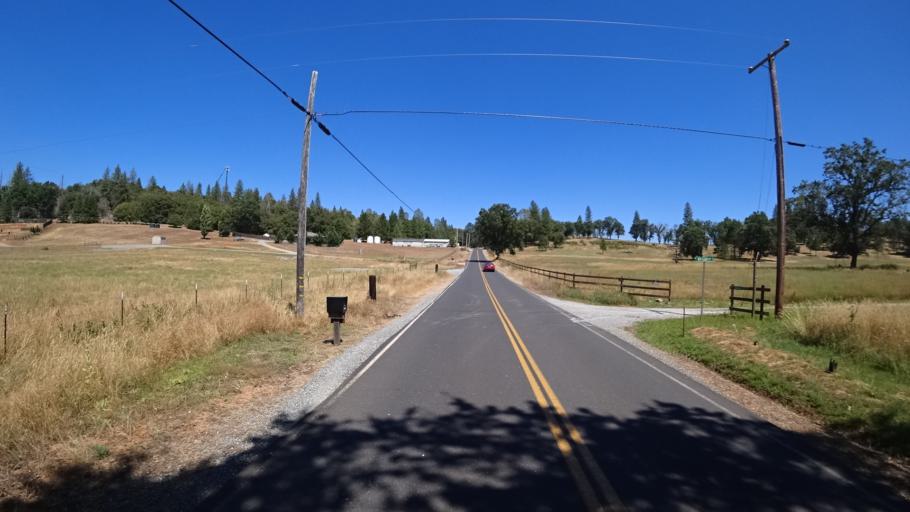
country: US
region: California
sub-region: Calaveras County
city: Mountain Ranch
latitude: 38.2841
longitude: -120.5143
